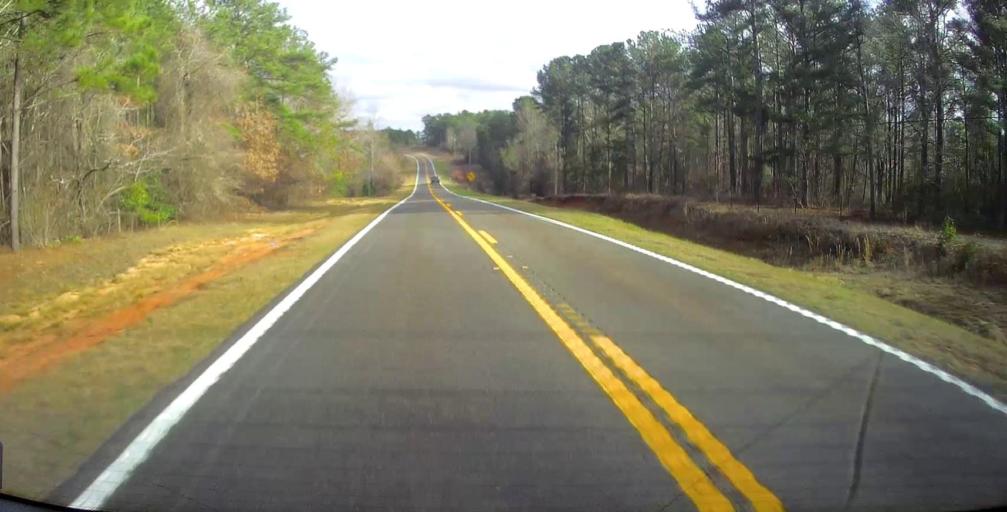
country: US
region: Georgia
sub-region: Marion County
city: Buena Vista
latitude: 32.4402
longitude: -84.5112
